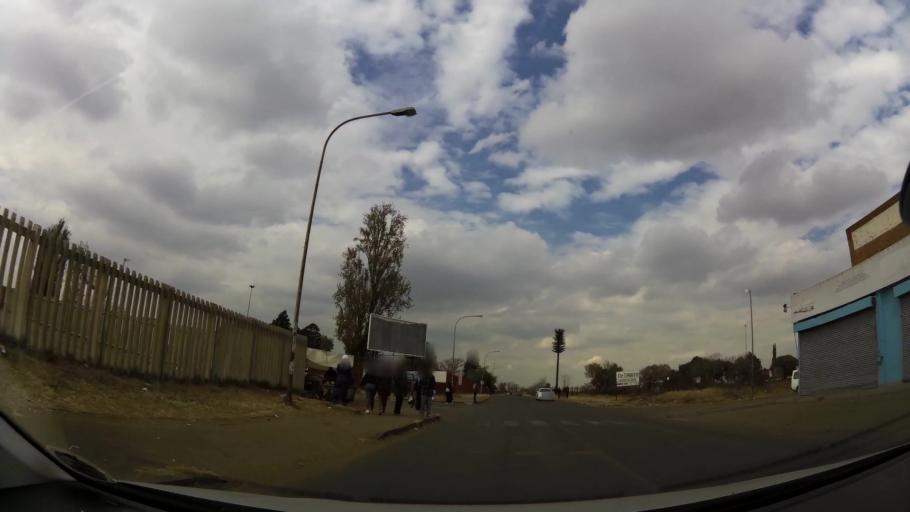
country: ZA
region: Gauteng
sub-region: City of Johannesburg Metropolitan Municipality
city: Soweto
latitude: -26.2712
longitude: 27.8561
